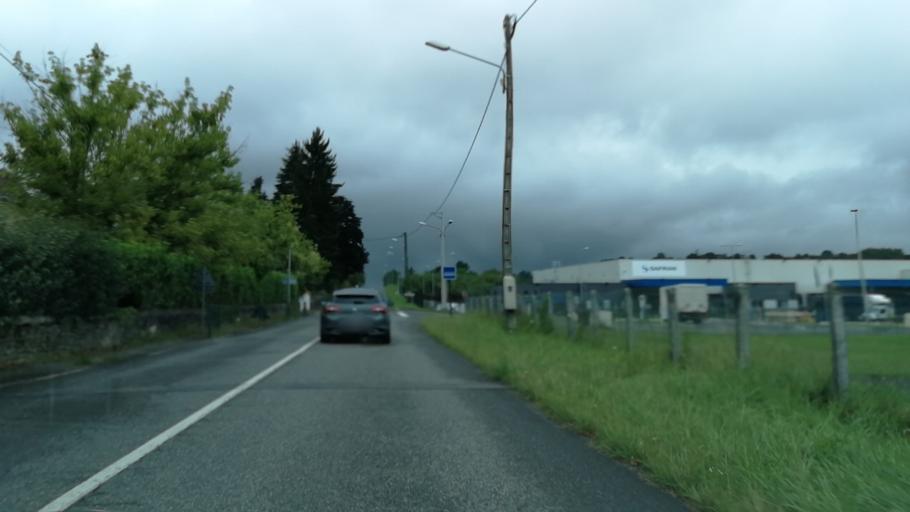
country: FR
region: Aquitaine
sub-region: Departement des Pyrenees-Atlantiques
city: Oloron-Sainte-Marie
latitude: 43.1685
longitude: -0.6023
